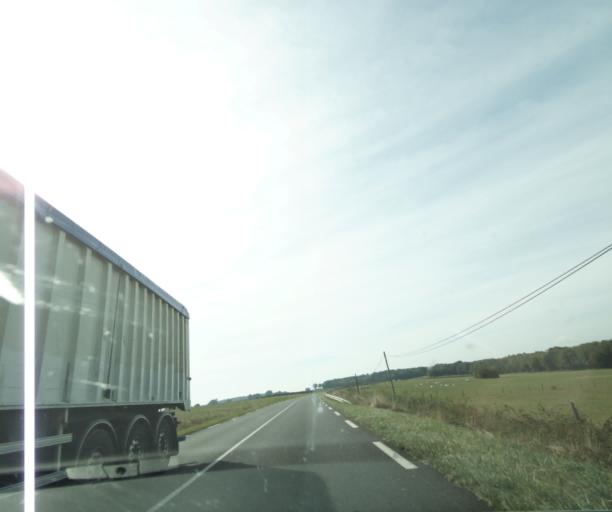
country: FR
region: Auvergne
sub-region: Departement de l'Allier
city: Molinet
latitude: 46.4480
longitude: 3.9152
